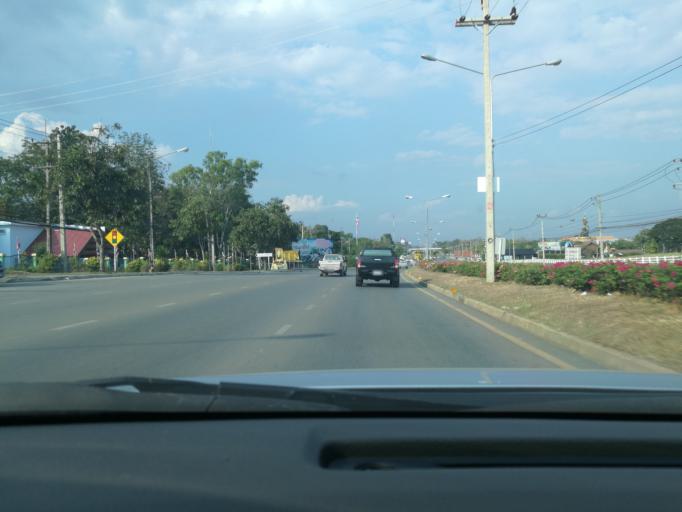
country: TH
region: Phetchabun
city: Phetchabun
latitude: 16.4429
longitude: 101.1514
